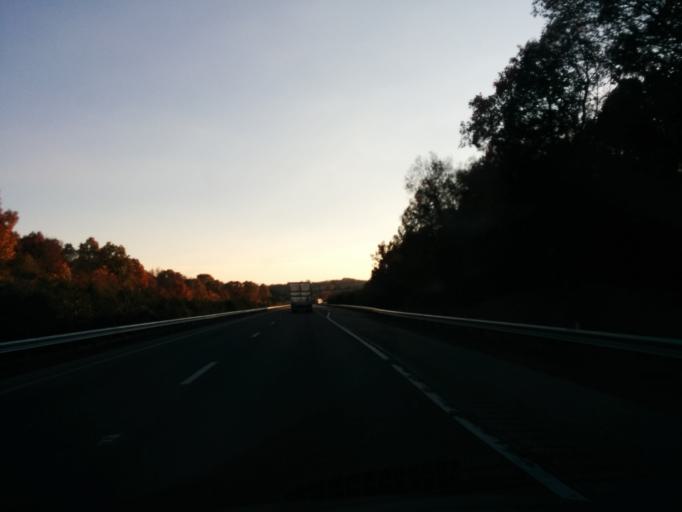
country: US
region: Virginia
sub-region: Rockbridge County
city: East Lexington
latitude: 37.8002
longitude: -79.3939
